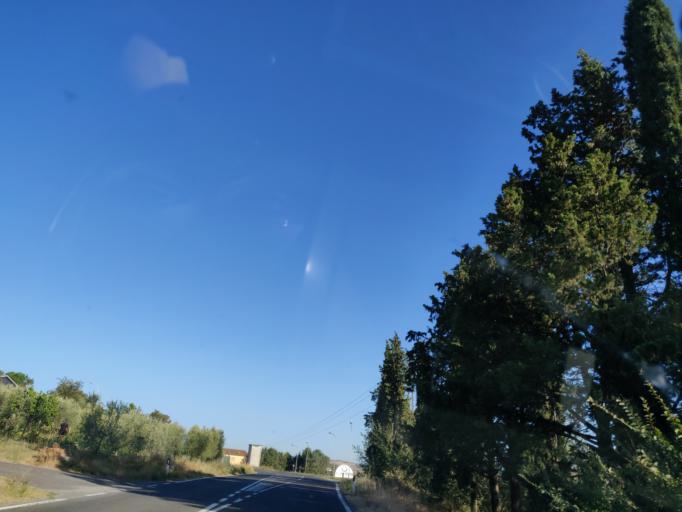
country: IT
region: Tuscany
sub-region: Provincia di Siena
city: Piancastagnaio
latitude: 42.8197
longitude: 11.7330
